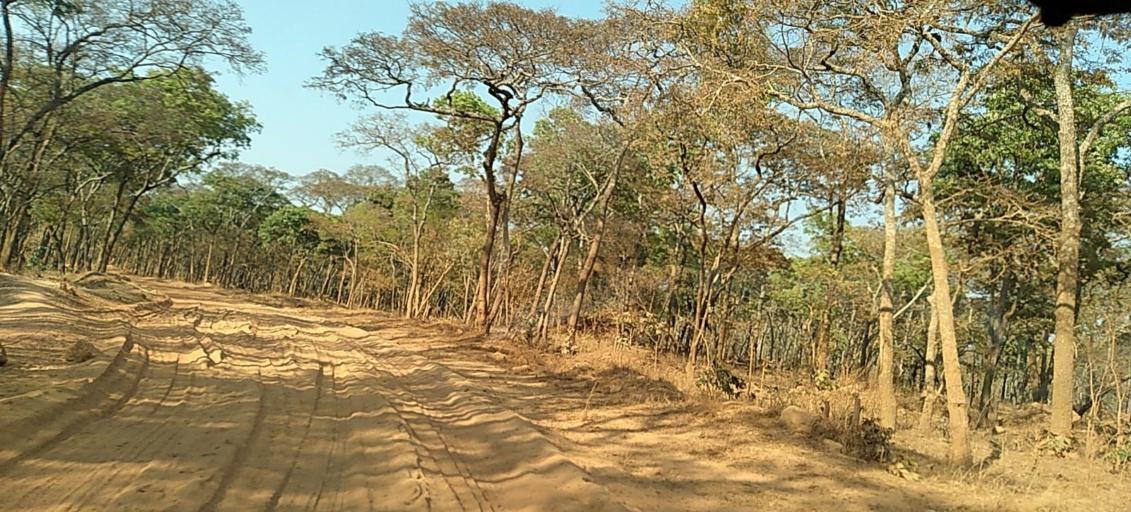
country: ZM
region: North-Western
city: Kasempa
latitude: -13.6037
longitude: 25.9775
